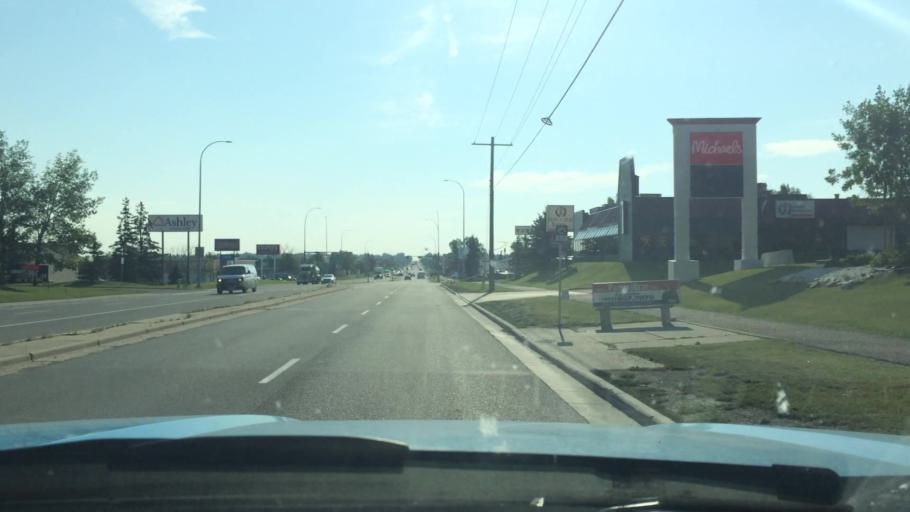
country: CA
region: Alberta
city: Calgary
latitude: 51.0814
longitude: -113.9946
